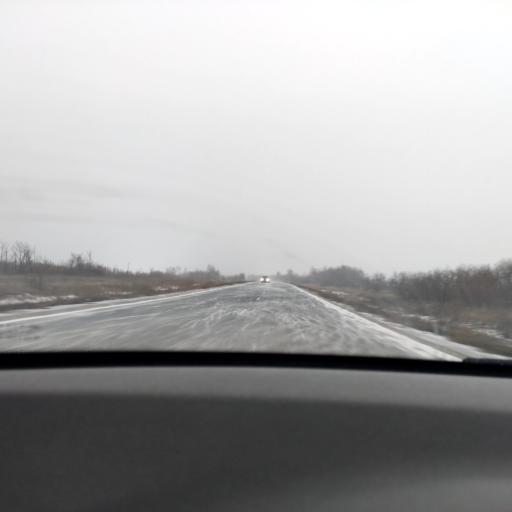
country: RU
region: Samara
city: Novokuybyshevsk
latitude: 52.9177
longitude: 49.9254
